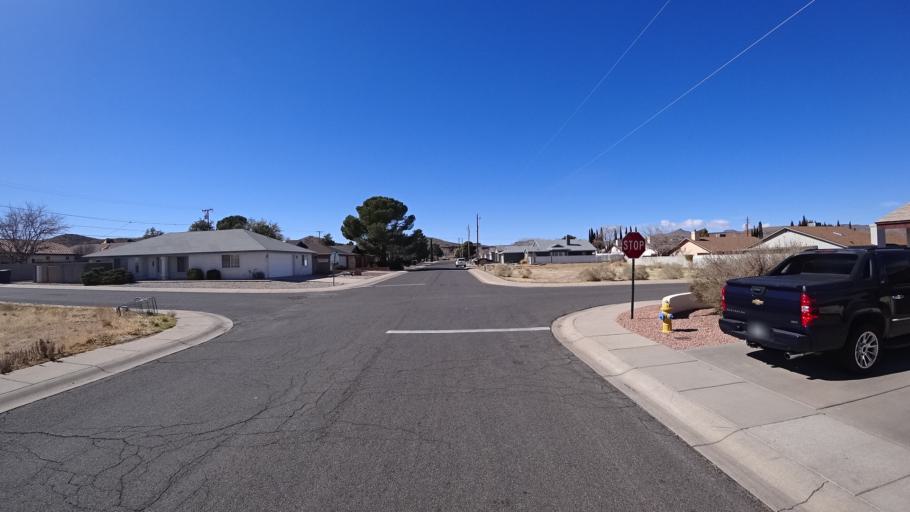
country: US
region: Arizona
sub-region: Mohave County
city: Kingman
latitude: 35.2076
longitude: -114.0377
